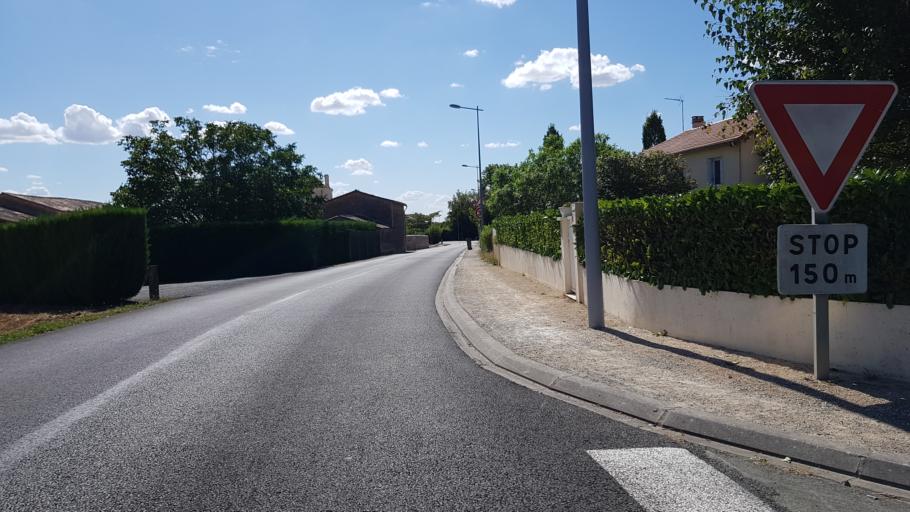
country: FR
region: Poitou-Charentes
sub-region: Departement des Deux-Sevres
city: Vouille
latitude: 46.3117
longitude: -0.3621
